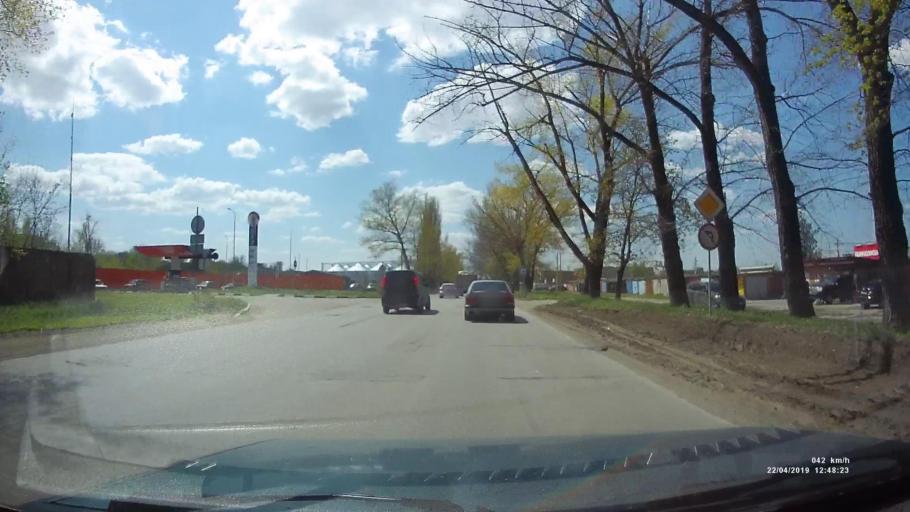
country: RU
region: Rostov
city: Azov
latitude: 47.0959
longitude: 39.4047
